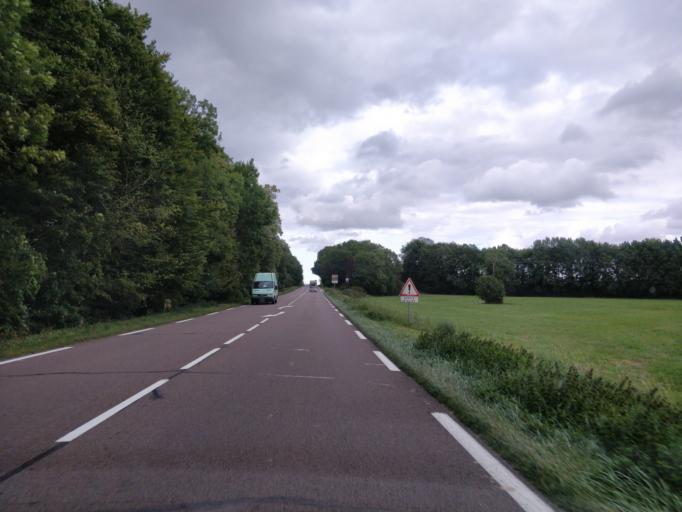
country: FR
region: Champagne-Ardenne
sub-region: Departement de l'Aube
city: Lusigny-sur-Barse
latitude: 48.2403
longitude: 4.3134
